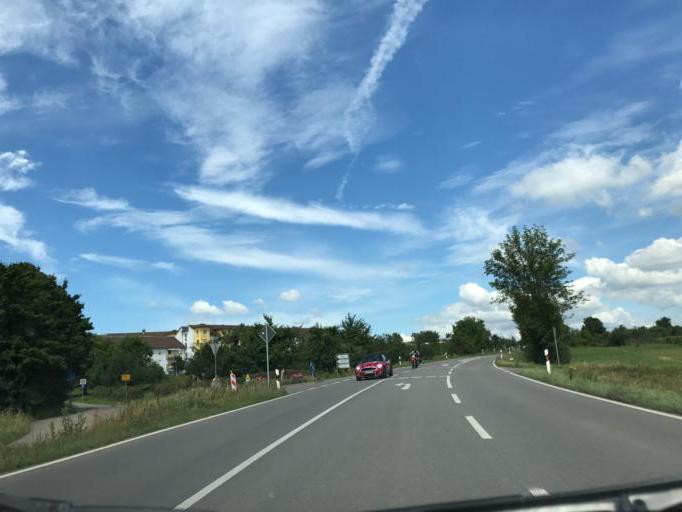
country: DE
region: Baden-Wuerttemberg
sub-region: Regierungsbezirk Stuttgart
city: Waiblingen
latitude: 48.8062
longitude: 9.3290
